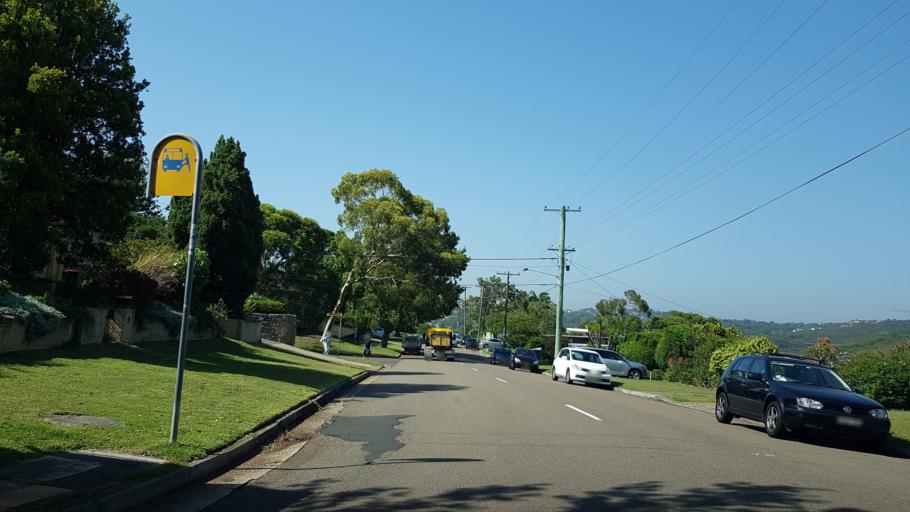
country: AU
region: New South Wales
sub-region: Warringah
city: Narrabeen
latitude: -33.7277
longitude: 151.2799
